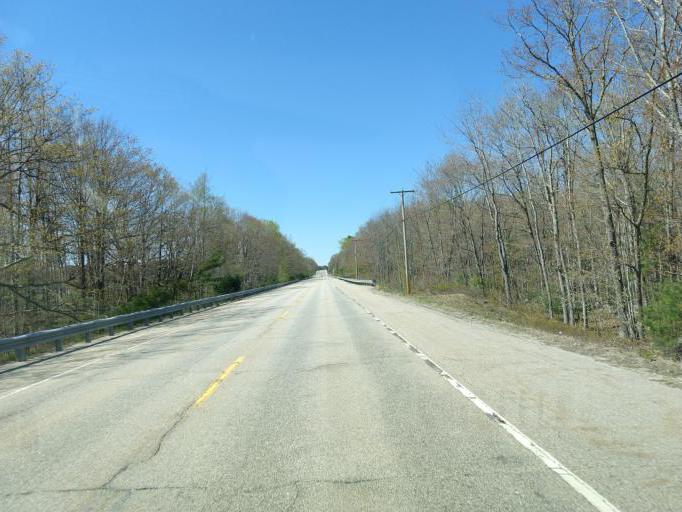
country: US
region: Maine
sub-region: York County
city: Old Orchard Beach
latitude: 43.4507
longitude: -70.3873
